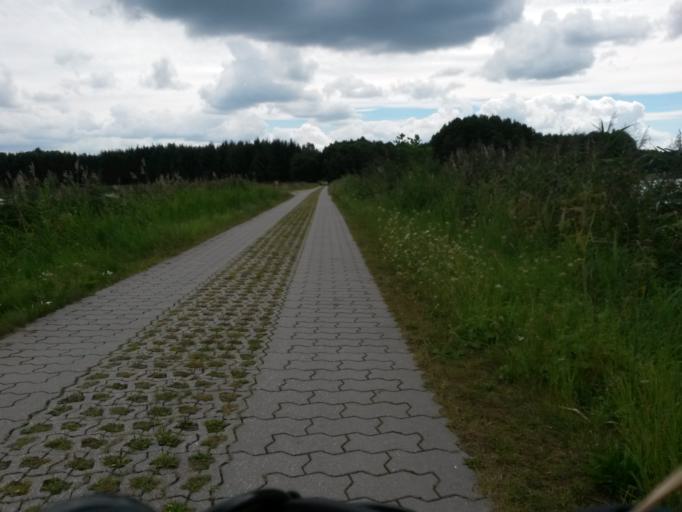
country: DE
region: Brandenburg
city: Angermunde
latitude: 53.0461
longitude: 13.9425
